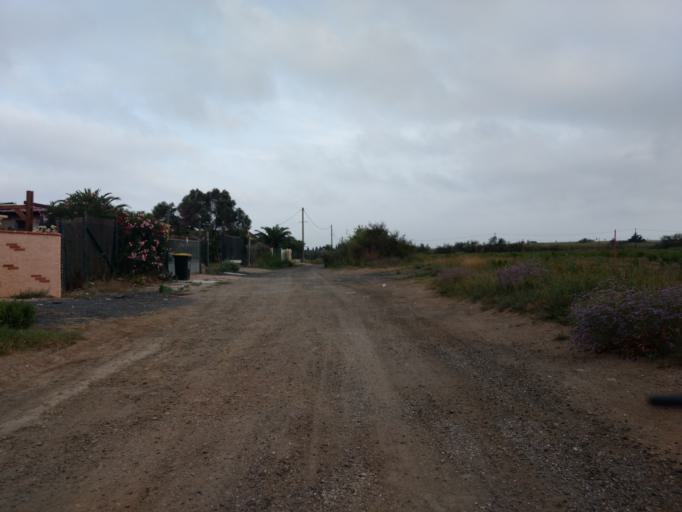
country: FR
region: Languedoc-Roussillon
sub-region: Departement des Pyrenees-Orientales
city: Le Barcares
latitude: 42.7828
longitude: 3.0167
